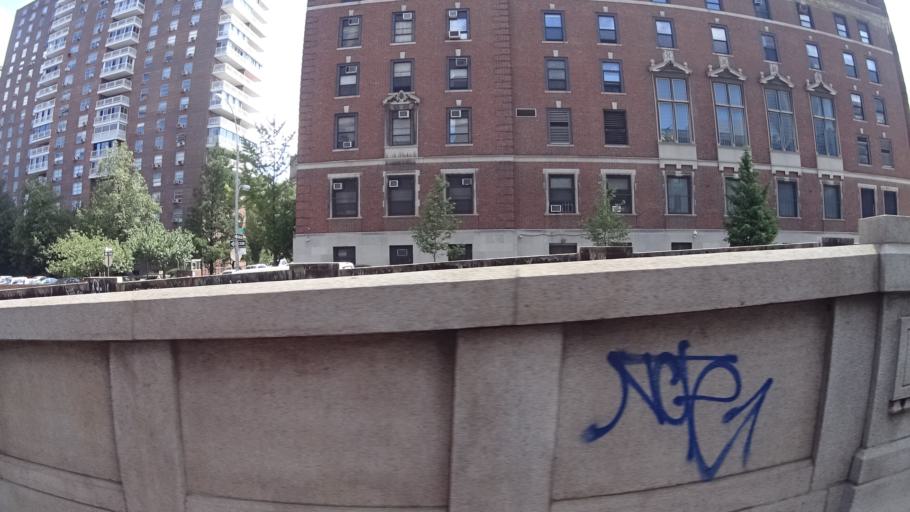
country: US
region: New Jersey
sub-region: Bergen County
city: Edgewater
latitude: 40.8124
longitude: -73.9608
